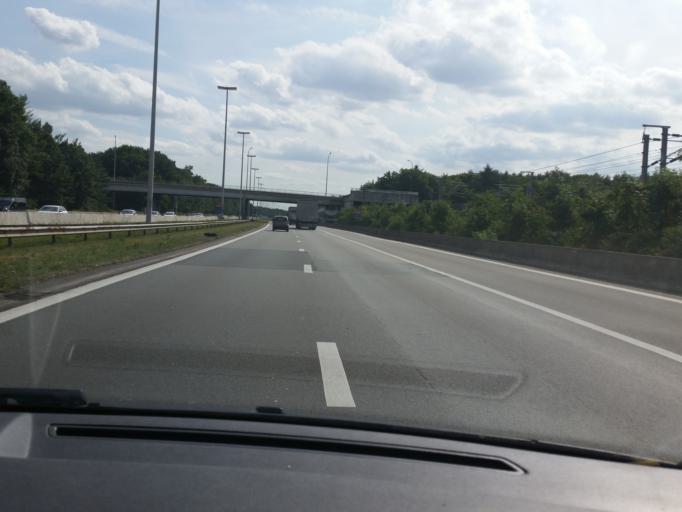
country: BE
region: Flanders
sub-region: Provincie Antwerpen
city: Brasschaat
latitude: 51.2847
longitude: 4.5126
